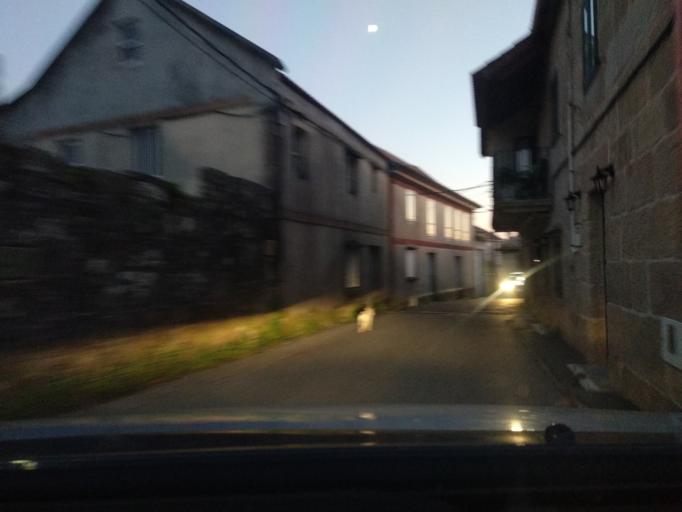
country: ES
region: Galicia
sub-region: Provincia de Pontevedra
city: Moana
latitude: 42.2850
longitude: -8.7492
